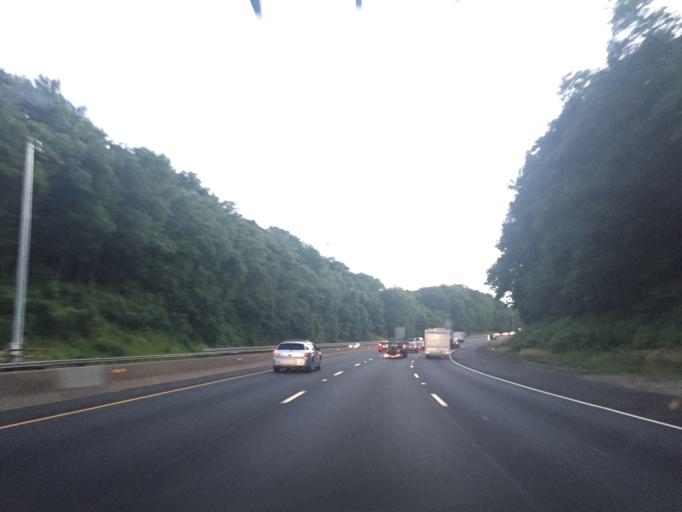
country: US
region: Maryland
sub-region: Harford County
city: Havre de Grace
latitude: 39.5774
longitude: -76.1133
